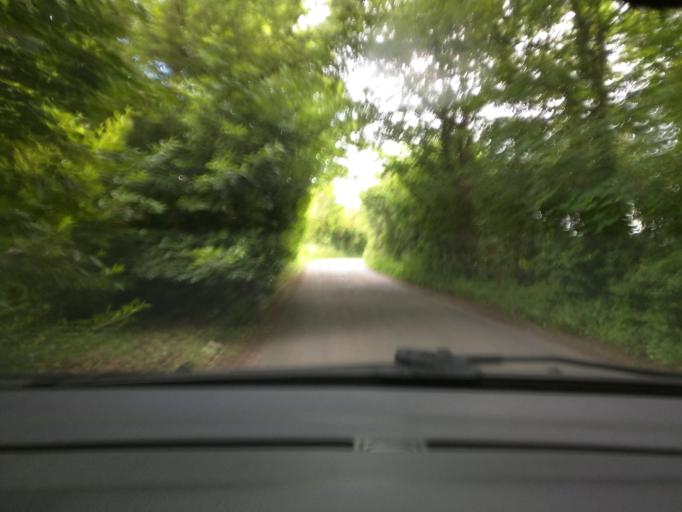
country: GB
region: England
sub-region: Suffolk
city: Saxmundham
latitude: 52.2282
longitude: 1.4656
